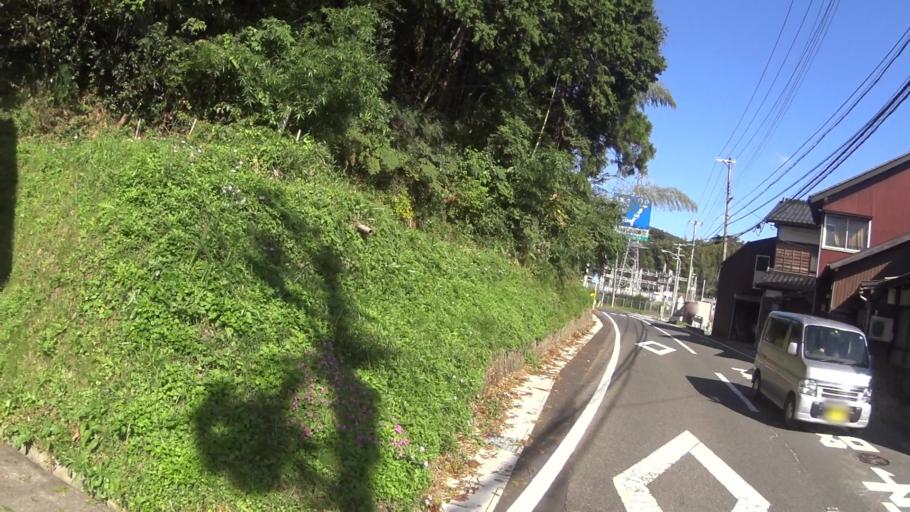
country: JP
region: Kyoto
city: Miyazu
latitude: 35.6743
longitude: 135.0815
